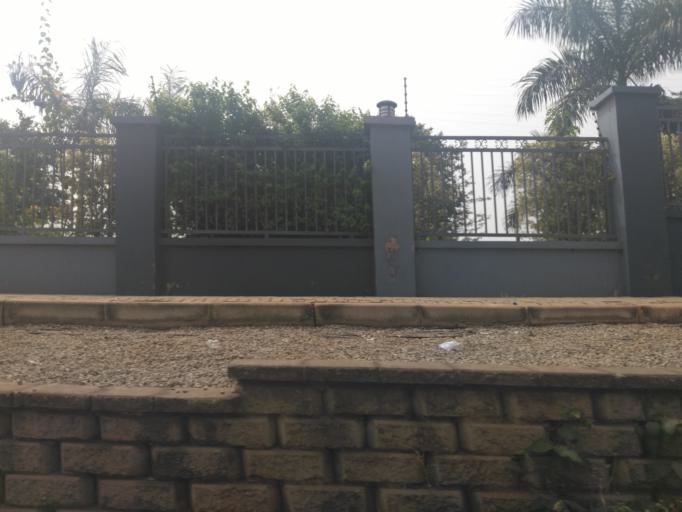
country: GH
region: Ashanti
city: Kumasi
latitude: 6.6812
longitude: -1.6244
